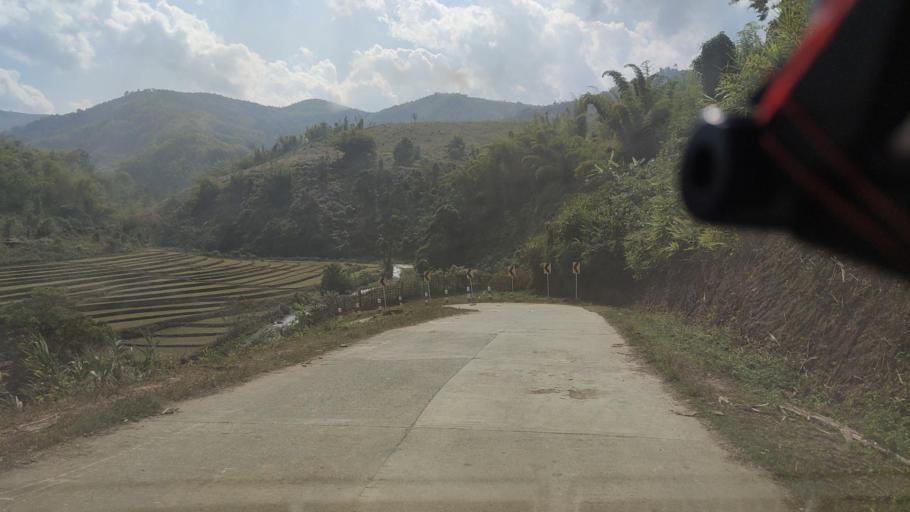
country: CN
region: Yunnan
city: Nayun
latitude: 21.9473
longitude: 98.8442
